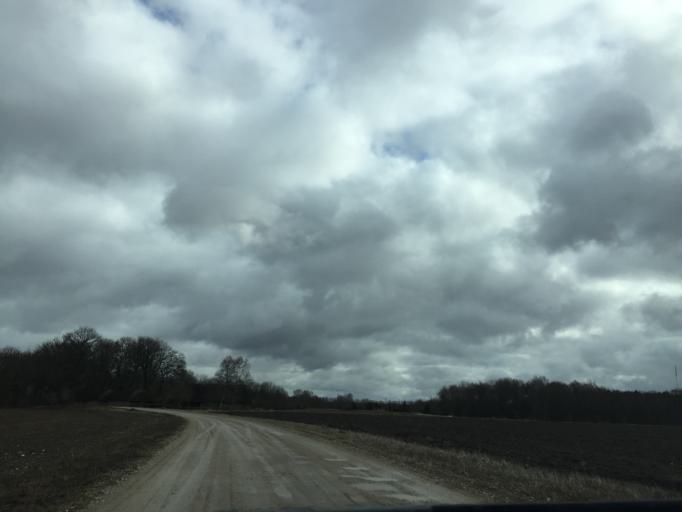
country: EE
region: Laeaene
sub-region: Ridala Parish
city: Uuemoisa
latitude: 58.6909
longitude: 23.5587
